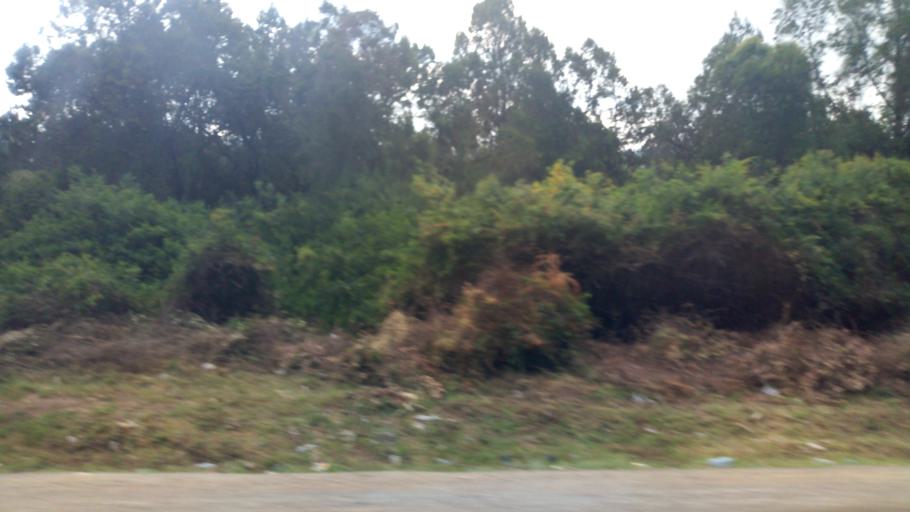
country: KE
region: Kiambu
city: Limuru
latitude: -1.0724
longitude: 36.6020
